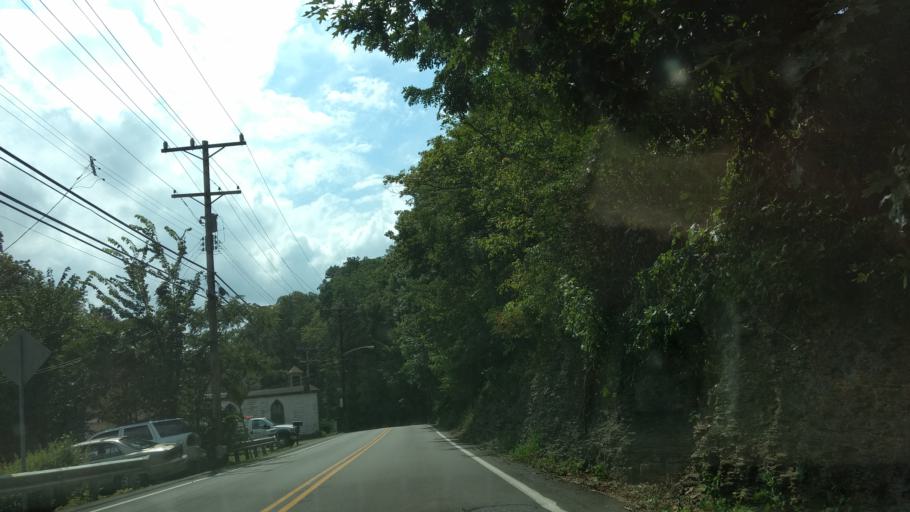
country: US
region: Pennsylvania
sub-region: Allegheny County
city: Bellevue
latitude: 40.5004
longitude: -80.0448
